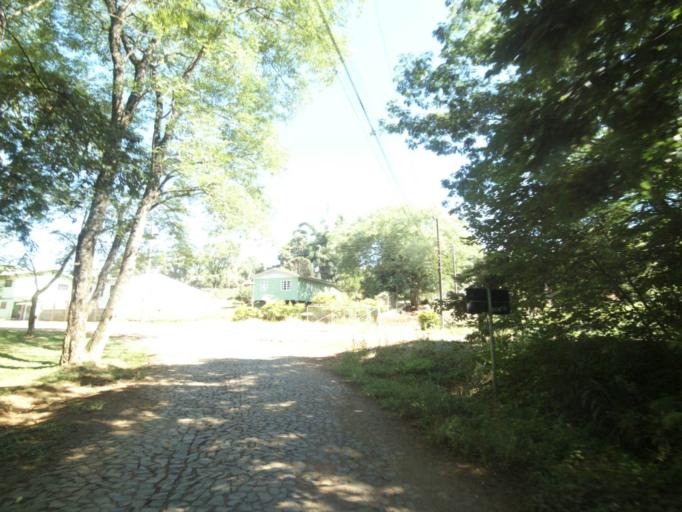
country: BR
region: Parana
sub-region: Ampere
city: Ampere
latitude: -26.1679
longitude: -53.3656
